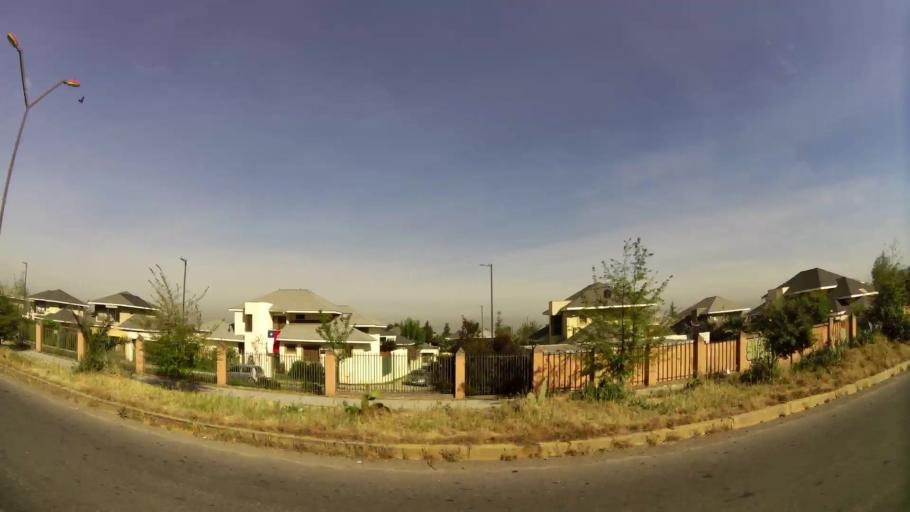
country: CL
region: Santiago Metropolitan
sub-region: Provincia de Santiago
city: Villa Presidente Frei, Nunoa, Santiago, Chile
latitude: -33.4918
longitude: -70.5503
